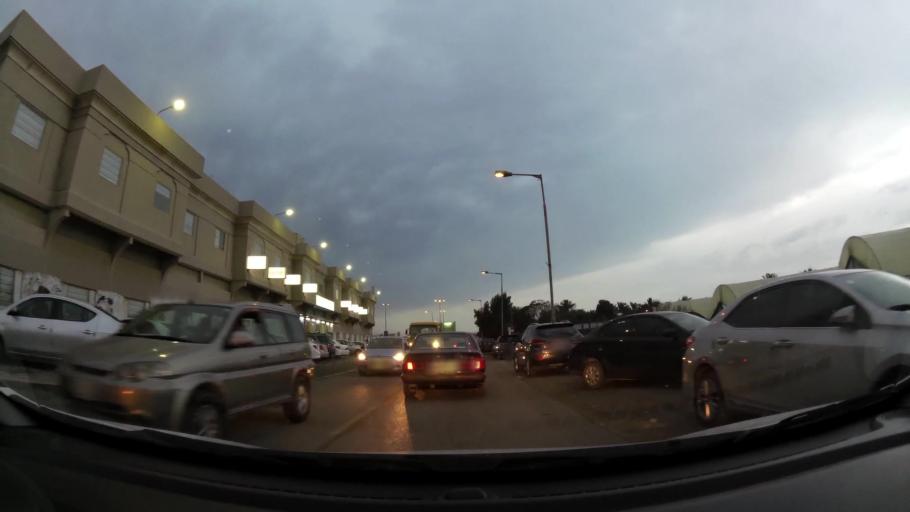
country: BH
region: Central Governorate
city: Madinat Hamad
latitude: 26.1452
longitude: 50.4943
